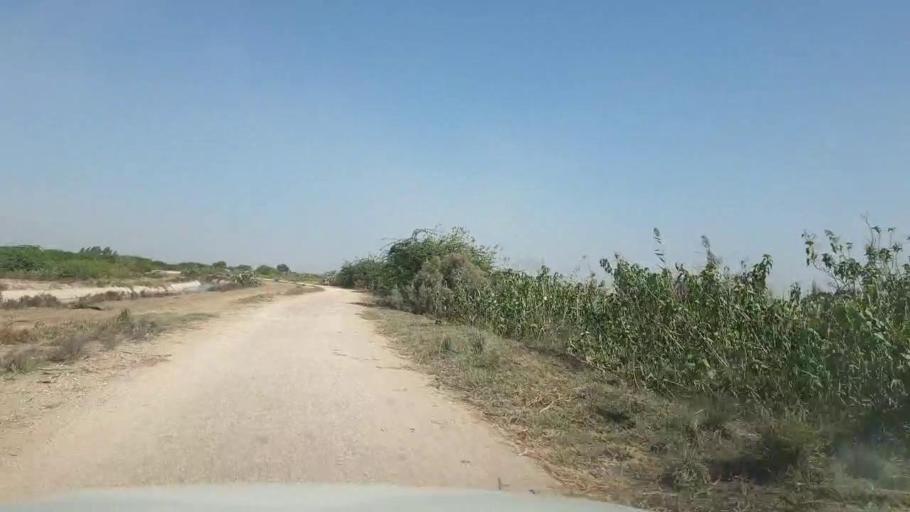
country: PK
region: Sindh
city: Mirpur Sakro
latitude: 24.4083
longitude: 67.7562
